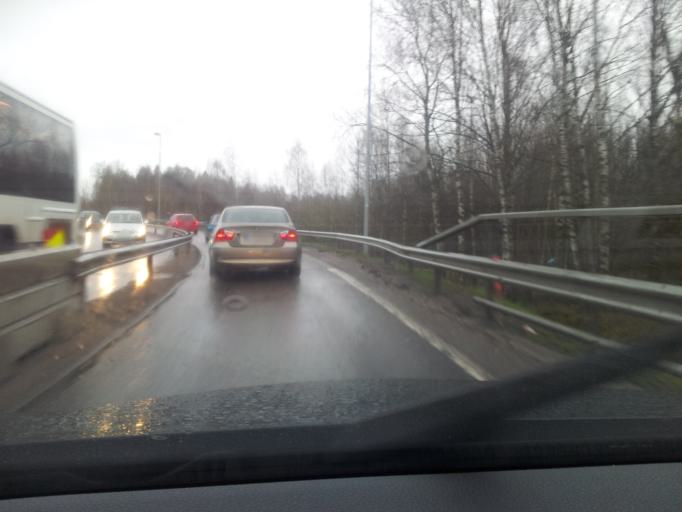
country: FI
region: Uusimaa
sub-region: Helsinki
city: Koukkuniemi
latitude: 60.1649
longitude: 24.7543
